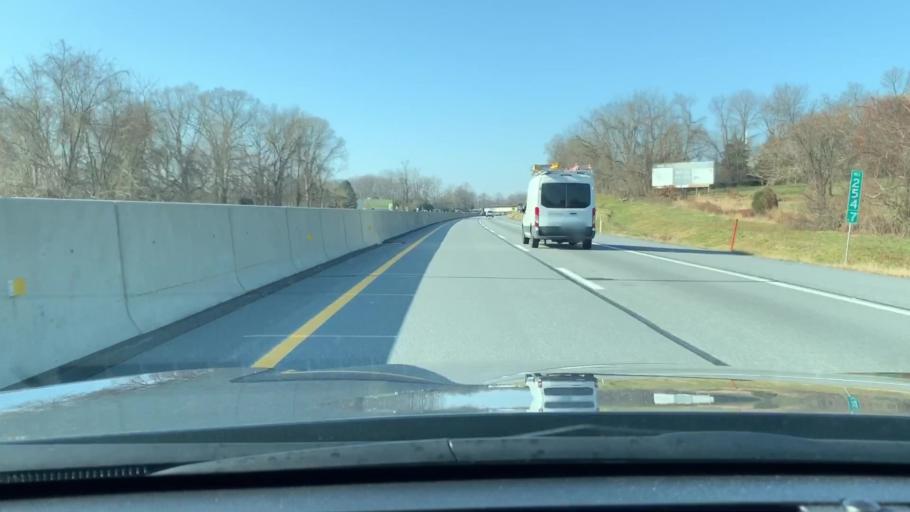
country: US
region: Pennsylvania
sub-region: Lancaster County
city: Elizabethtown
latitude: 40.2077
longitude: -76.6509
